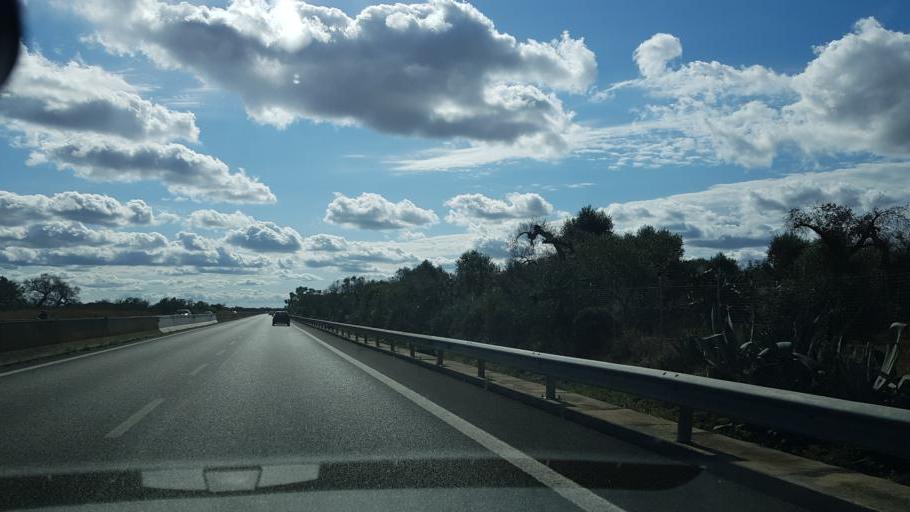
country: IT
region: Apulia
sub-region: Provincia di Lecce
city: Trepuzzi
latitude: 40.4135
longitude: 18.1025
